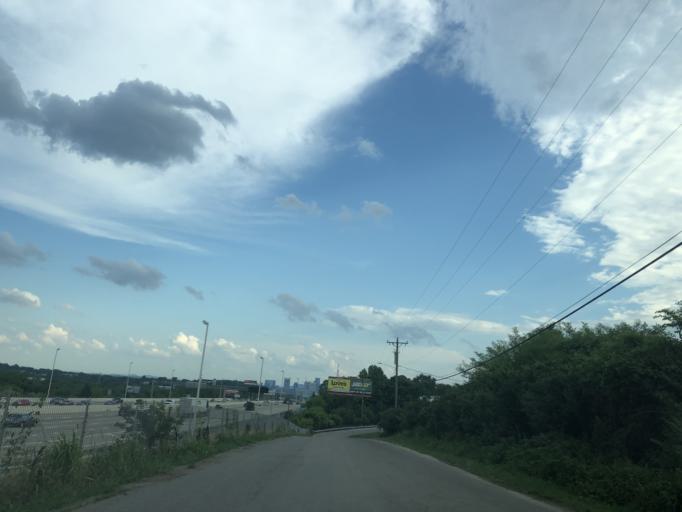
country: US
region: Tennessee
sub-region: Davidson County
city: Nashville
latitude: 36.2160
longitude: -86.7757
